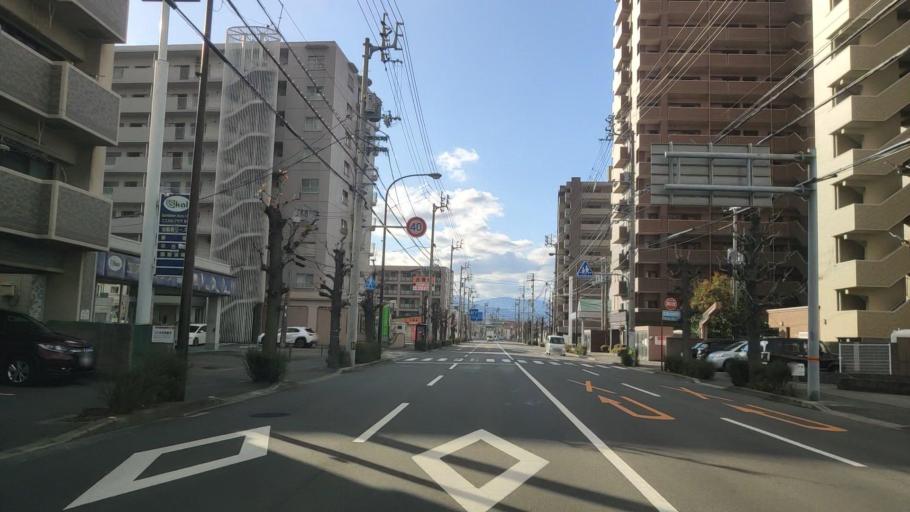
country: JP
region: Ehime
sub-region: Shikoku-chuo Shi
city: Matsuyama
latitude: 33.8324
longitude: 132.7524
